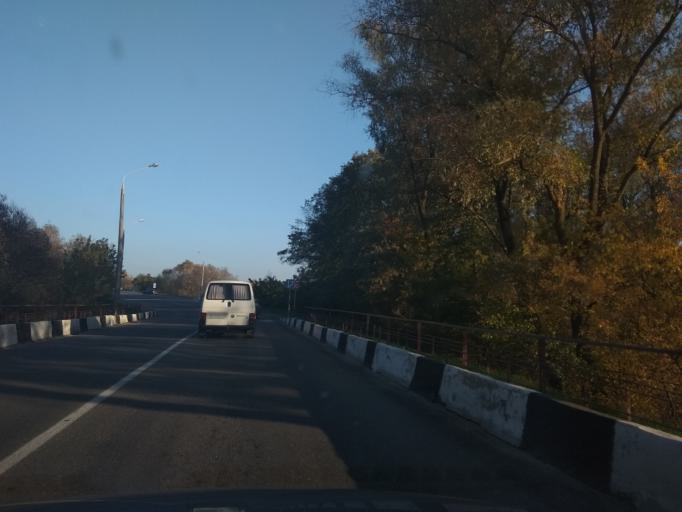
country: BY
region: Grodnenskaya
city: Vawkavysk
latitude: 53.1512
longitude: 24.4199
